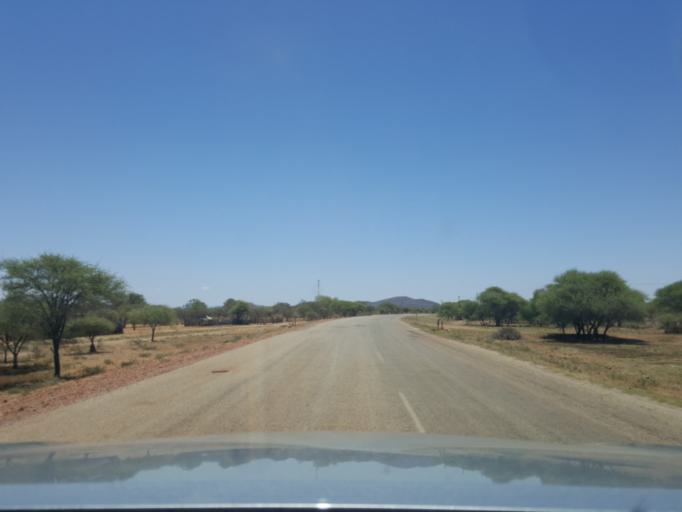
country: BW
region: South East
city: Ramotswa
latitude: -24.9932
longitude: 25.8987
